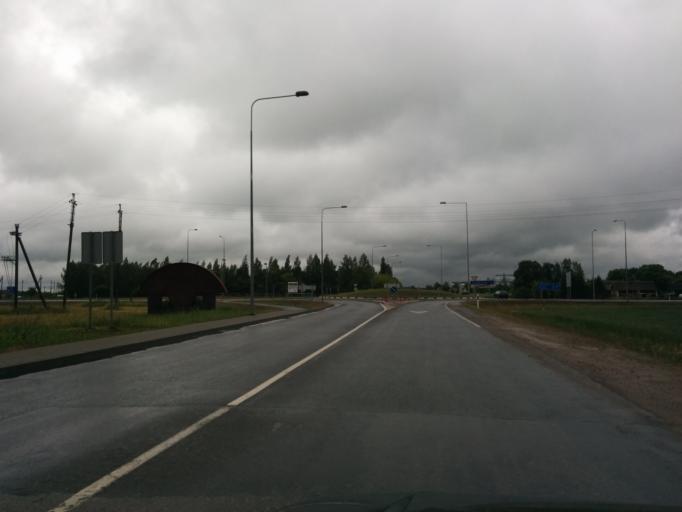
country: LT
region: Panevezys
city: Pasvalys
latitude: 56.0558
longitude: 24.4085
